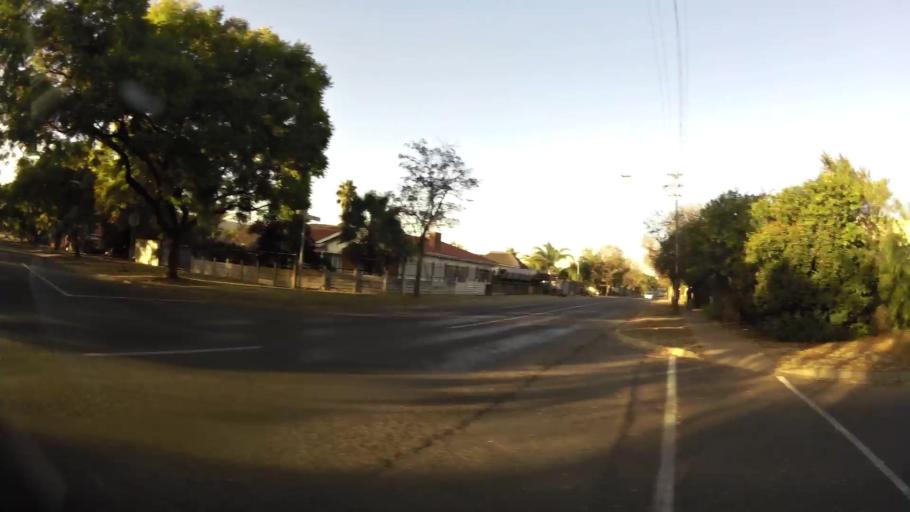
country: ZA
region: Gauteng
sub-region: City of Tshwane Metropolitan Municipality
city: Pretoria
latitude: -25.7119
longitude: 28.2207
